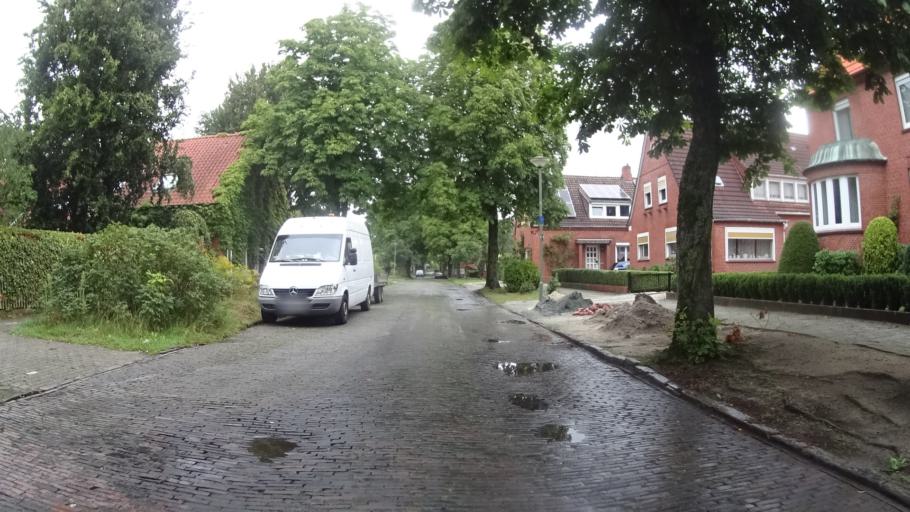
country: DE
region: Lower Saxony
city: Leer
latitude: 53.2332
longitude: 7.4452
